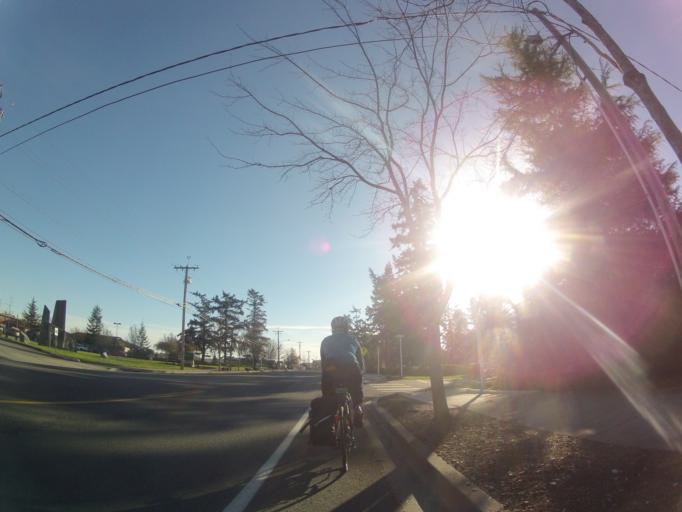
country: US
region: Washington
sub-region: Island County
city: Coupeville
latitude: 48.2144
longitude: -122.6862
